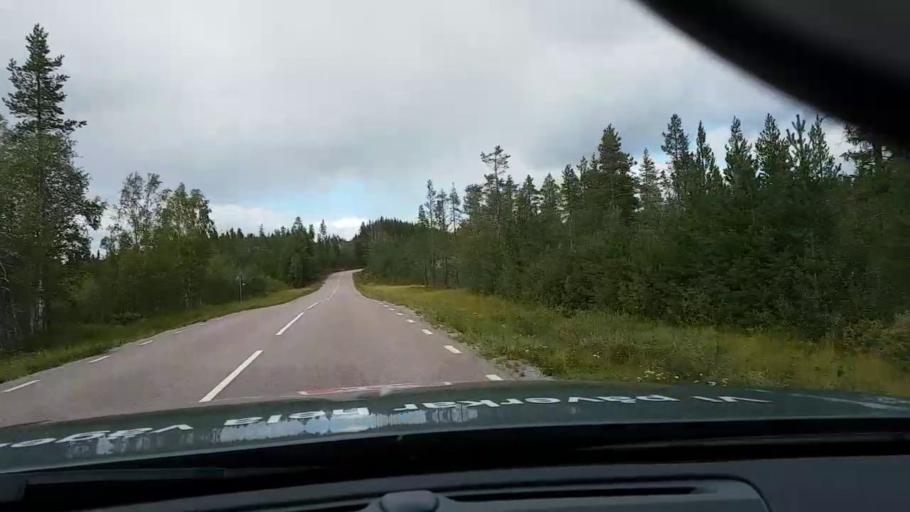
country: SE
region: Vaesterbotten
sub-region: Asele Kommun
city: Asele
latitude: 63.8693
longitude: 17.3584
